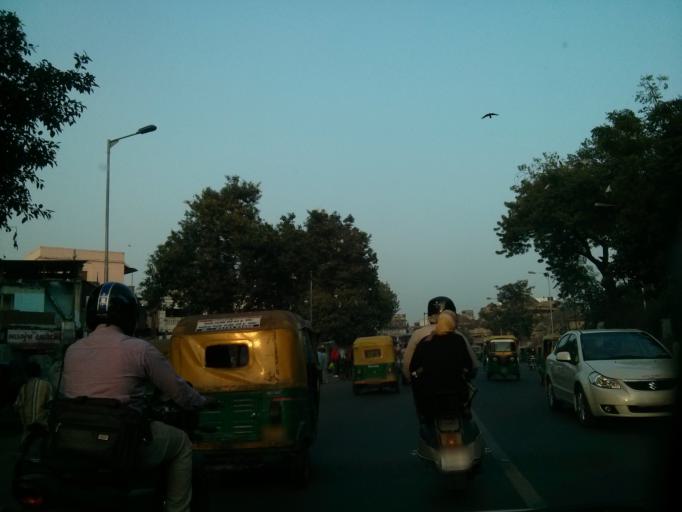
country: IN
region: Gujarat
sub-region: Ahmadabad
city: Ahmedabad
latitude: 23.0349
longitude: 72.5862
